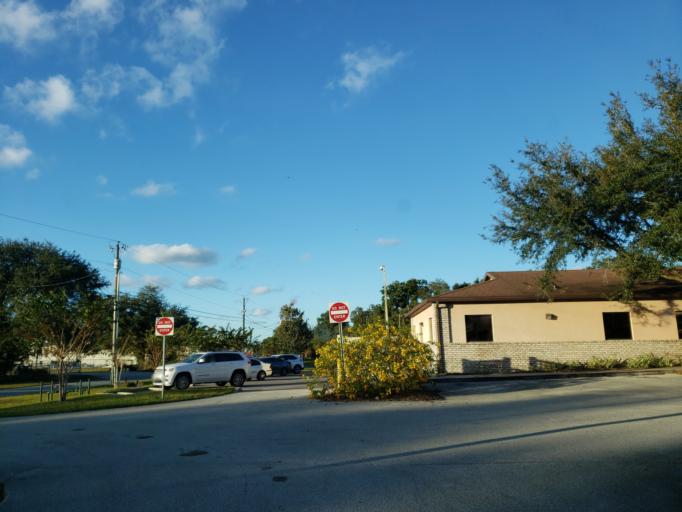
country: US
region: Florida
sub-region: Polk County
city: Lakeland Highlands
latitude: 27.9587
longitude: -81.9582
